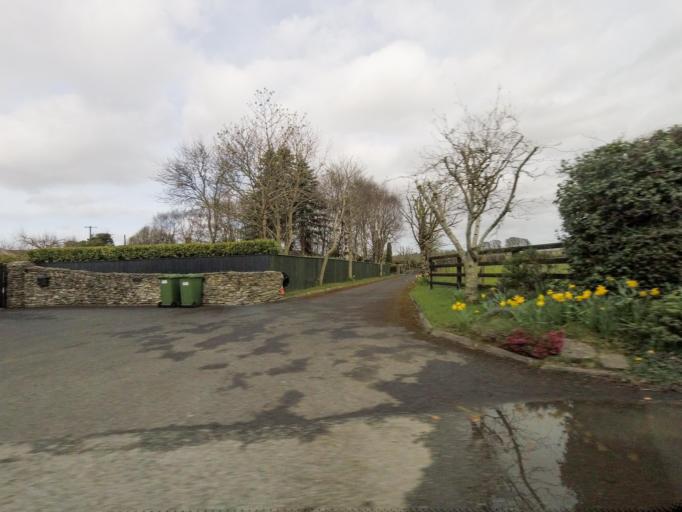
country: IE
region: Leinster
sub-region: Kildare
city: Naas
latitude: 53.1905
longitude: -6.6451
